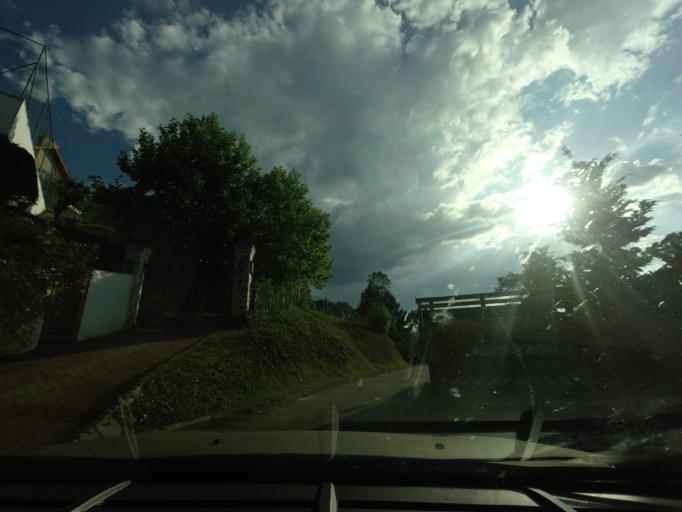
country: BR
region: Sao Paulo
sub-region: Campos Do Jordao
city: Campos do Jordao
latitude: -22.7194
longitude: -45.5553
